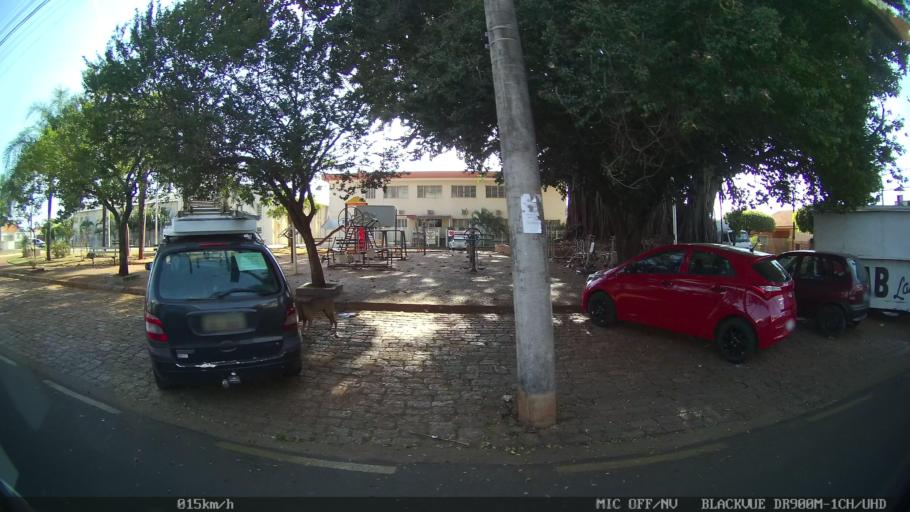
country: BR
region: Sao Paulo
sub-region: Sao Jose Do Rio Preto
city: Sao Jose do Rio Preto
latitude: -20.7945
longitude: -49.3833
